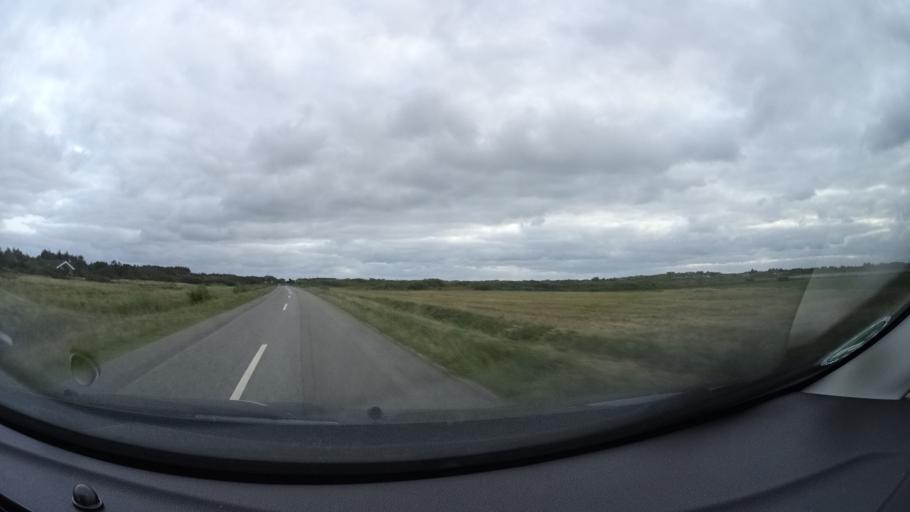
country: DK
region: Central Jutland
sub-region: Ringkobing-Skjern Kommune
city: Ringkobing
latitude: 56.1473
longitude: 8.1337
